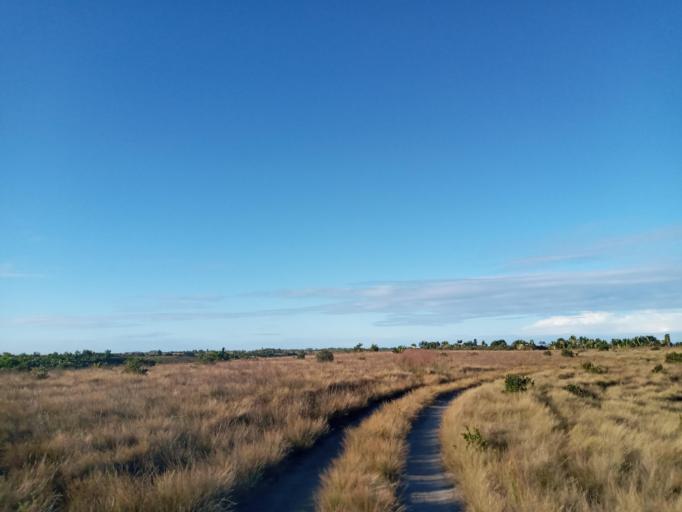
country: MG
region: Anosy
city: Fort Dauphin
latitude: -24.4305
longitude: 47.2948
